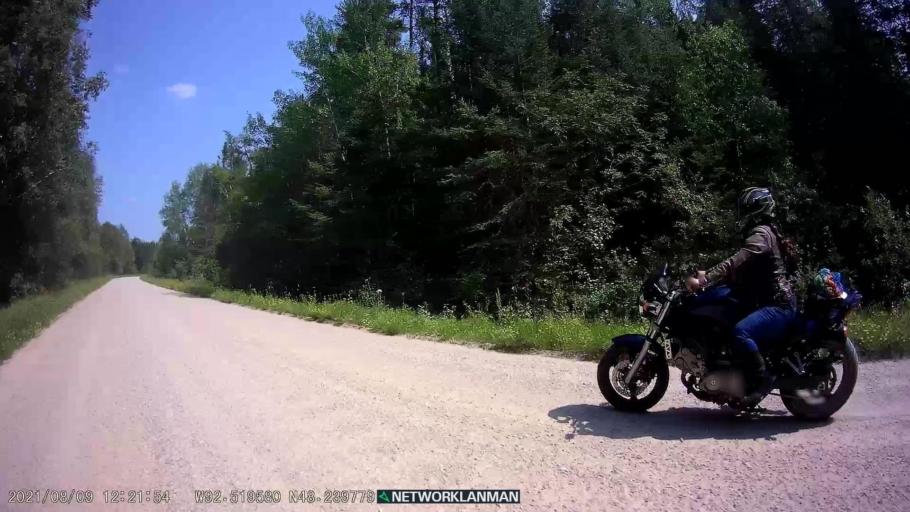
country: US
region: Minnesota
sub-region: Saint Louis County
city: Parkville
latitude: 48.2398
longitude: -92.5193
